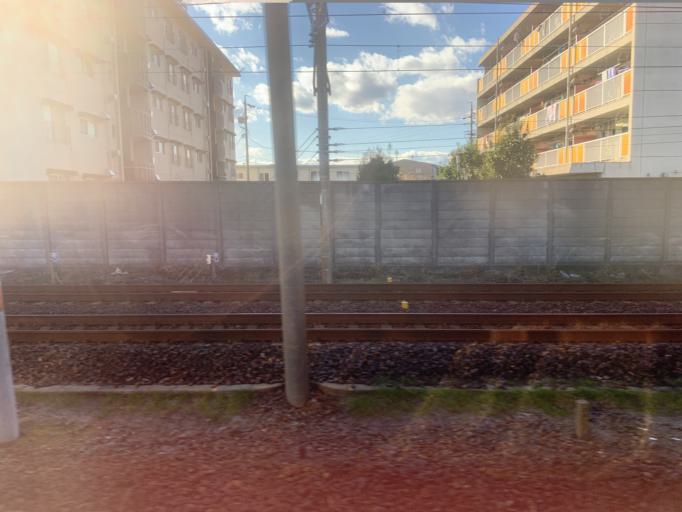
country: JP
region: Aichi
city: Ichinomiya
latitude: 35.3140
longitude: 136.7915
